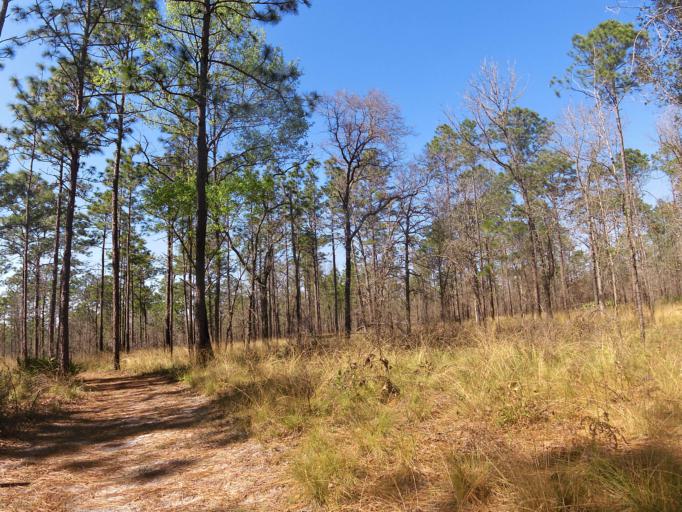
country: US
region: Florida
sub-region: Clay County
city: Middleburg
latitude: 30.1403
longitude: -81.8856
